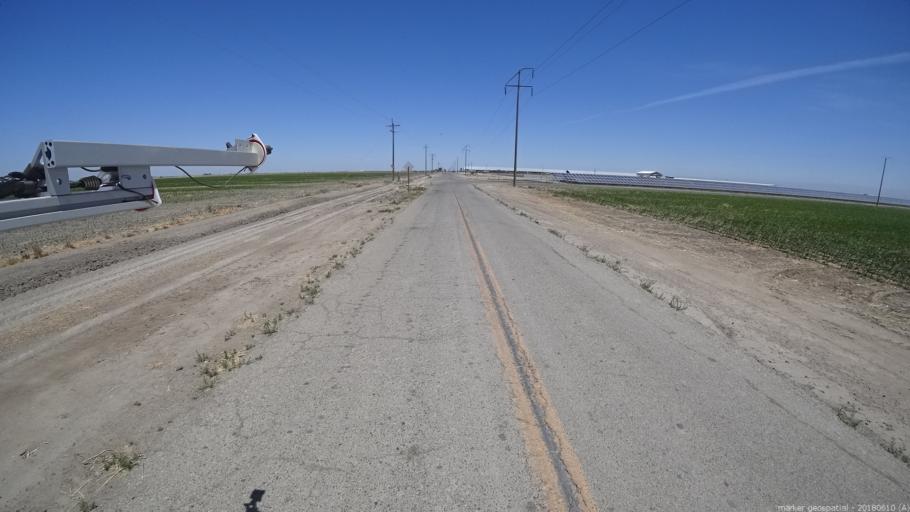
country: US
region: California
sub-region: Merced County
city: Dos Palos
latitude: 37.0538
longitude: -120.5286
